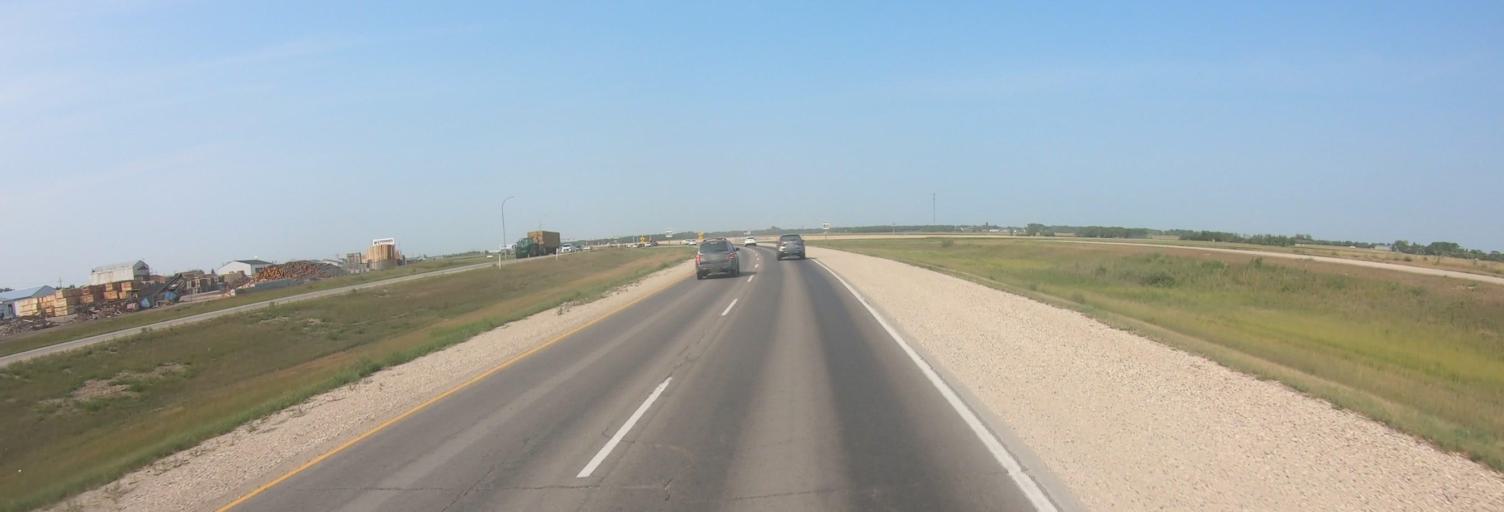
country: CA
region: Manitoba
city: Steinbach
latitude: 49.6002
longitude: -96.6840
